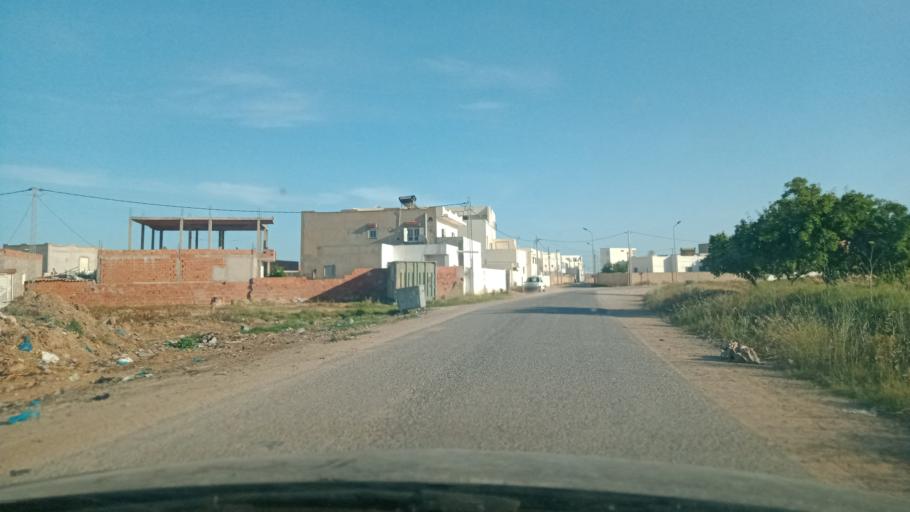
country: TN
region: Safaqis
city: Sfax
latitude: 34.8255
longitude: 10.7357
